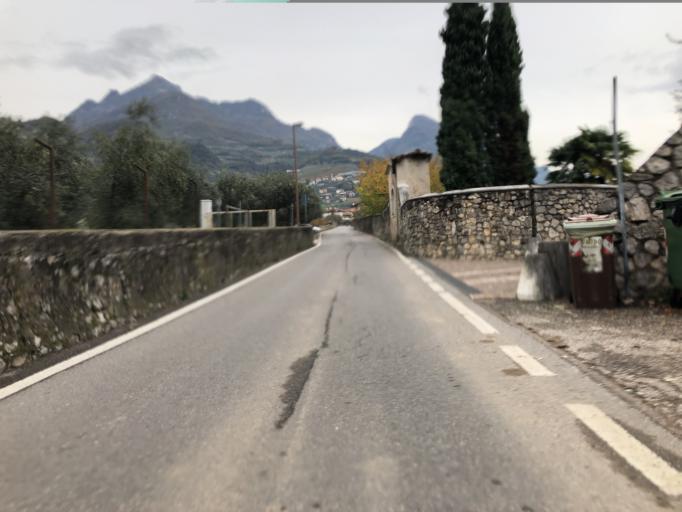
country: IT
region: Trentino-Alto Adige
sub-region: Provincia di Trento
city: Riva del Garda
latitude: 45.9022
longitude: 10.8392
